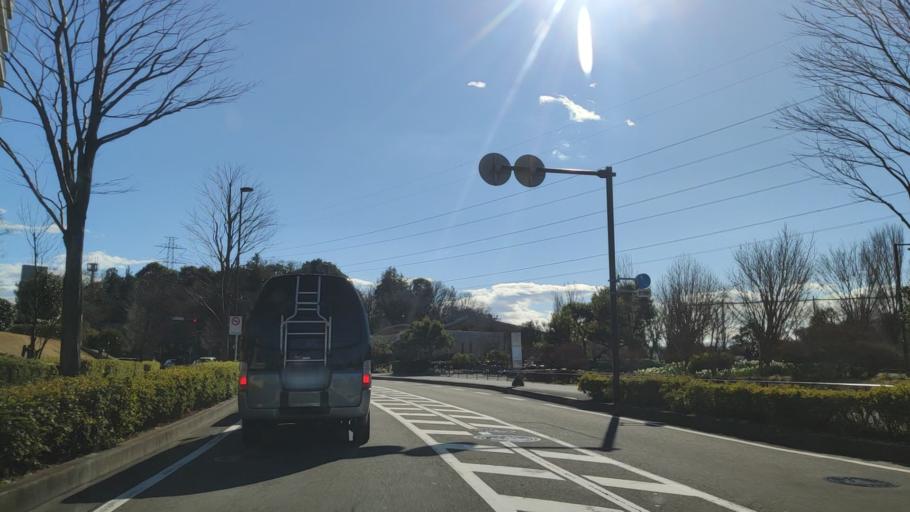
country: JP
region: Tokyo
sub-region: Machida-shi
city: Machida
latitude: 35.5192
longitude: 139.4967
